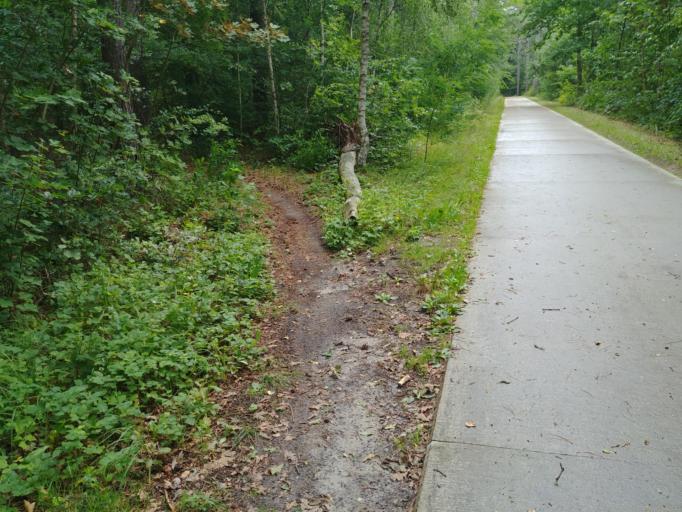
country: NL
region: North Holland
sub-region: Gemeente Bergen
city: Egmond aan Zee
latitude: 52.6823
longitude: 4.6674
